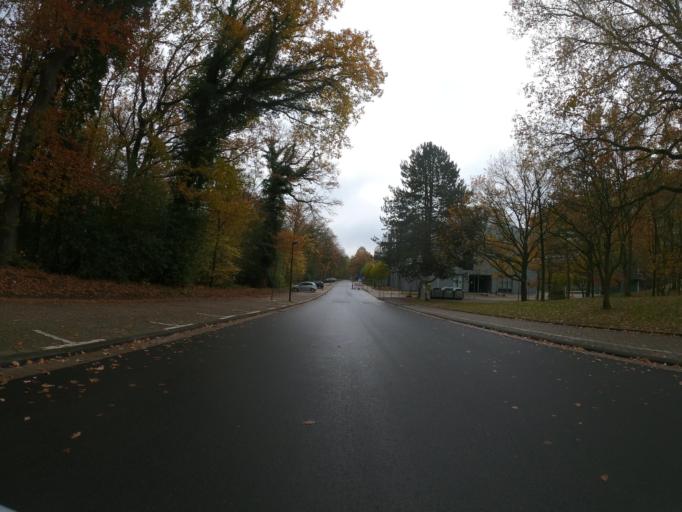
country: DE
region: North Rhine-Westphalia
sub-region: Regierungsbezirk Arnsberg
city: Bochum
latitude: 51.4466
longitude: 7.2679
